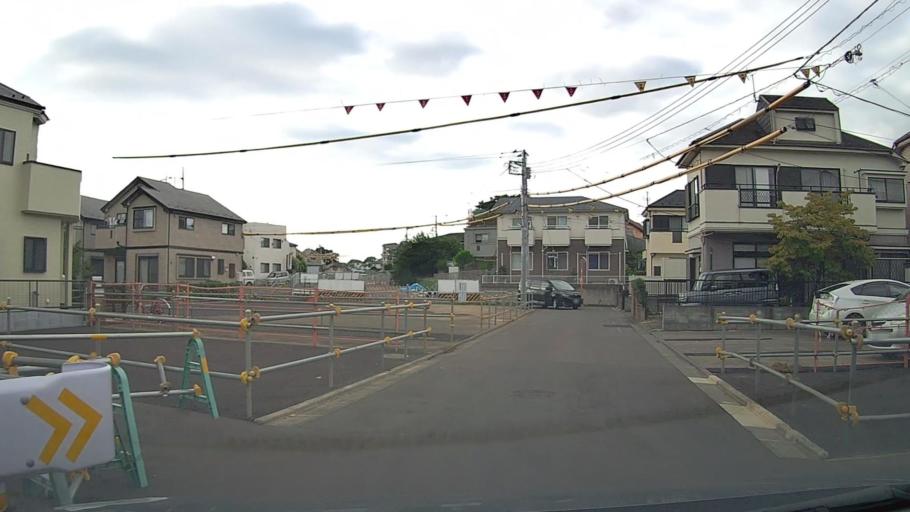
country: JP
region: Tokyo
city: Higashimurayama-shi
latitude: 35.7528
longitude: 139.4895
